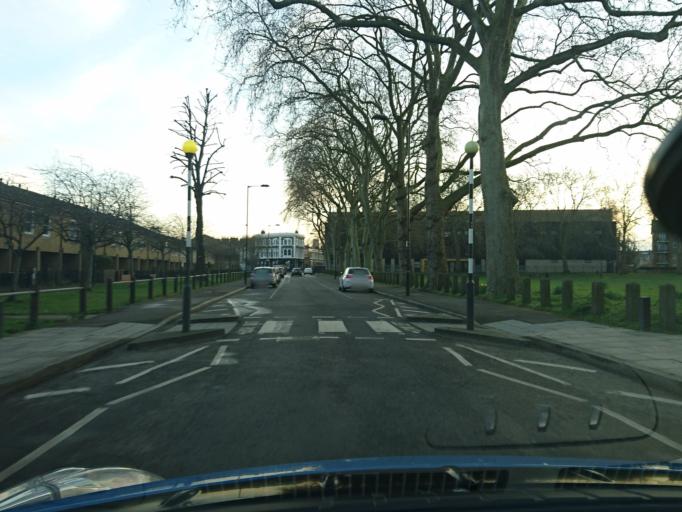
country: GB
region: England
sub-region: Greater London
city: Hackney
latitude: 51.5401
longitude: -0.0399
